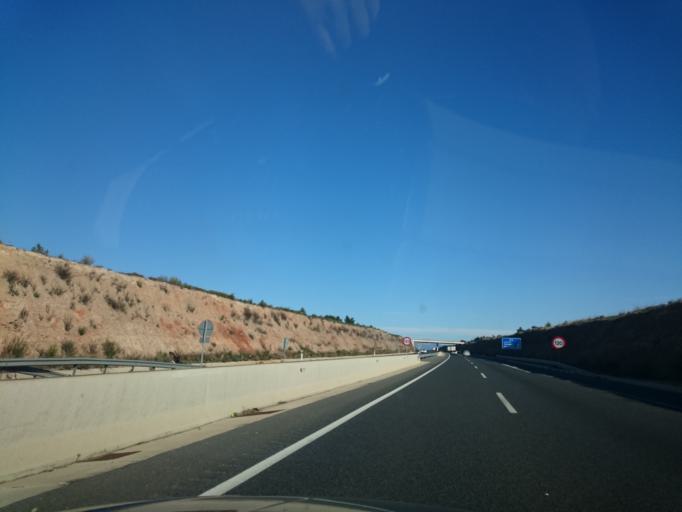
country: ES
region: Catalonia
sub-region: Provincia de Tarragona
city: Colldejou
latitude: 41.0079
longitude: 0.9187
